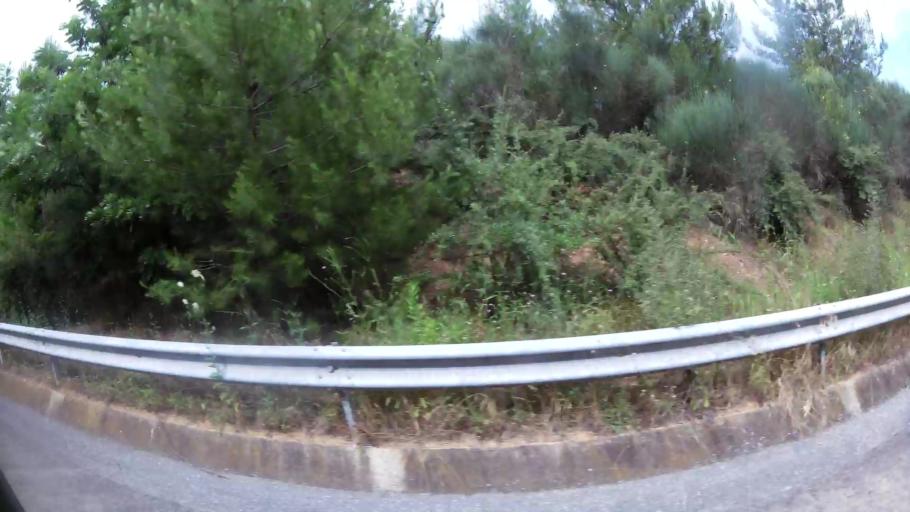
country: GR
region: Central Macedonia
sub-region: Nomos Pierias
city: Makrygialos
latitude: 40.4183
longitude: 22.5915
